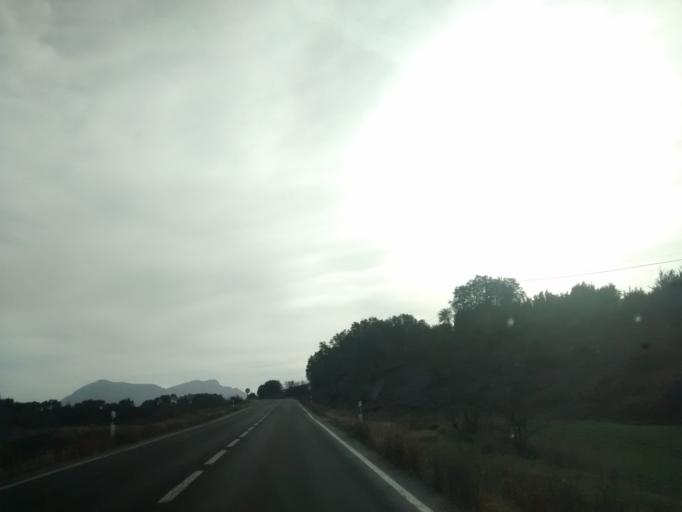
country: ES
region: Aragon
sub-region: Provincia de Huesca
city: Bailo
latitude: 42.5824
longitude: -0.8293
